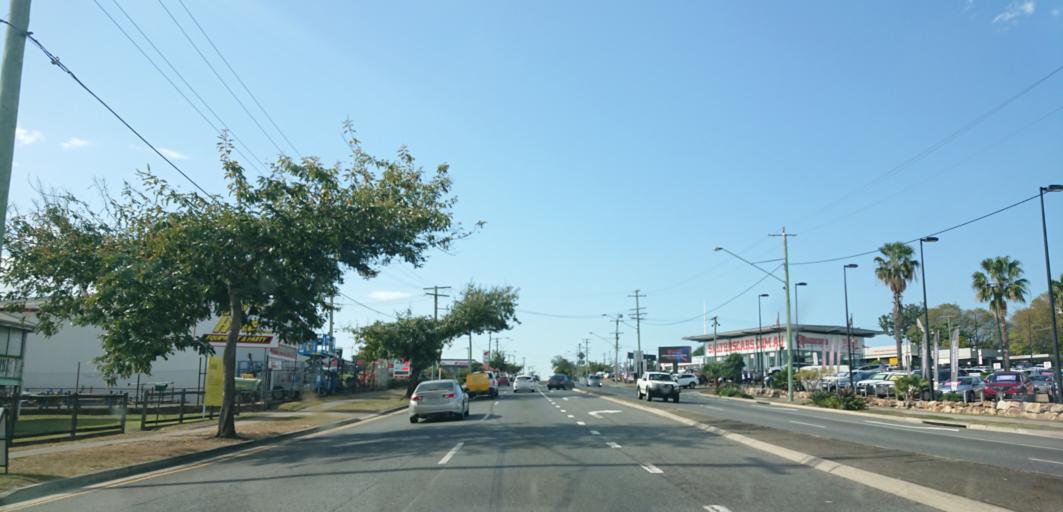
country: AU
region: Queensland
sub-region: Brisbane
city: Yeerongpilly
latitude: -27.5328
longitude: 153.0164
